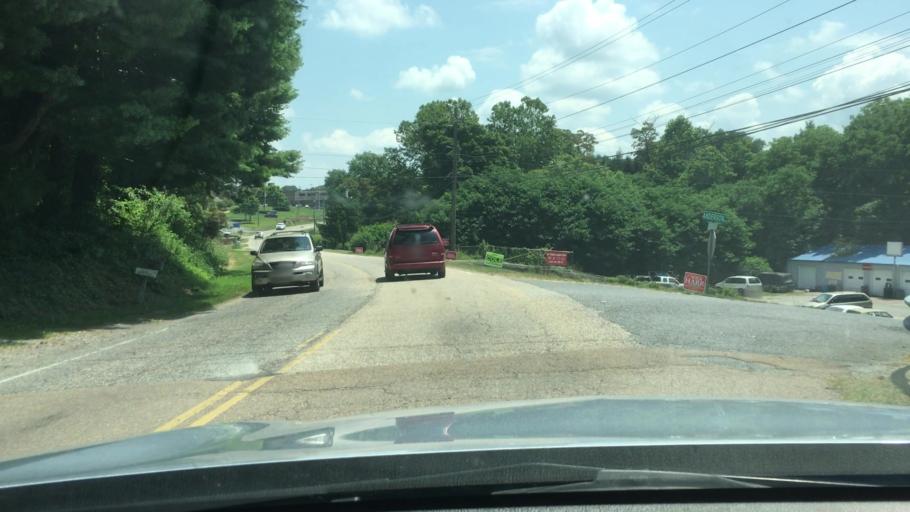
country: US
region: Tennessee
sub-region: Sullivan County
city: Blountville
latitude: 36.5350
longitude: -82.3262
